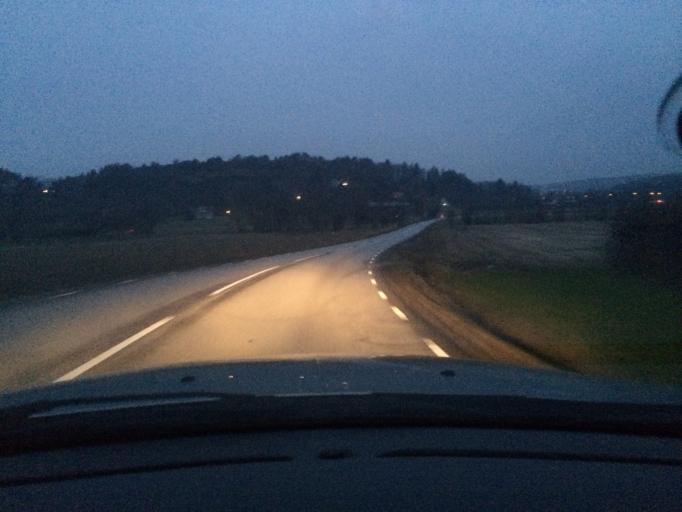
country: SE
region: Vaestra Goetaland
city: Svanesund
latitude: 58.1279
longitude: 11.8551
